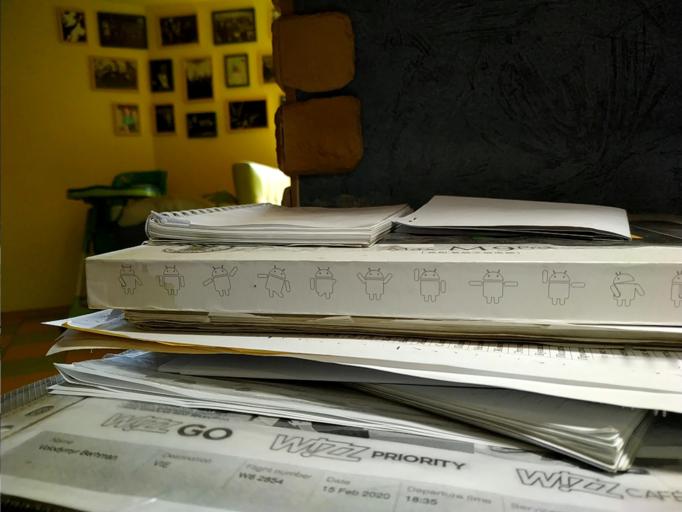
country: RU
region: Pskov
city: Plyussa
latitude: 58.4416
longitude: 29.6353
